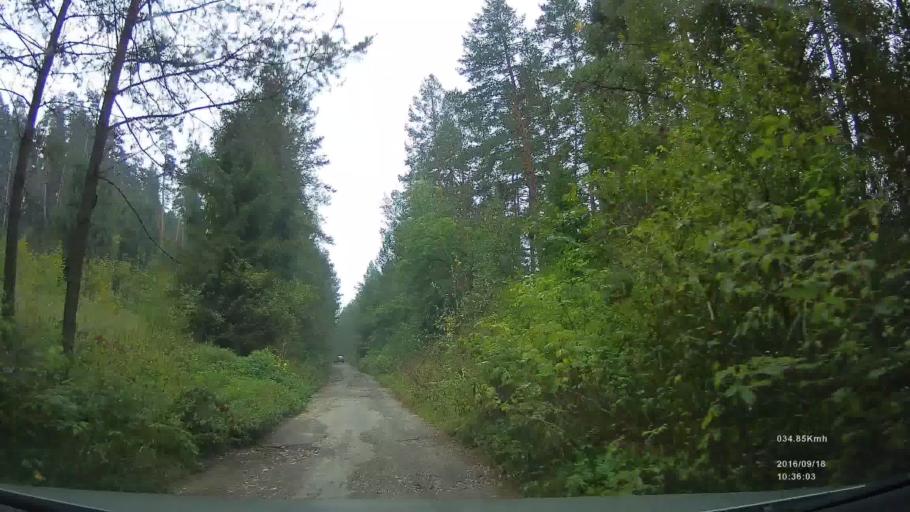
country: SK
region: Kosicky
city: Spisska Nova Ves
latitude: 48.9601
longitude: 20.6235
